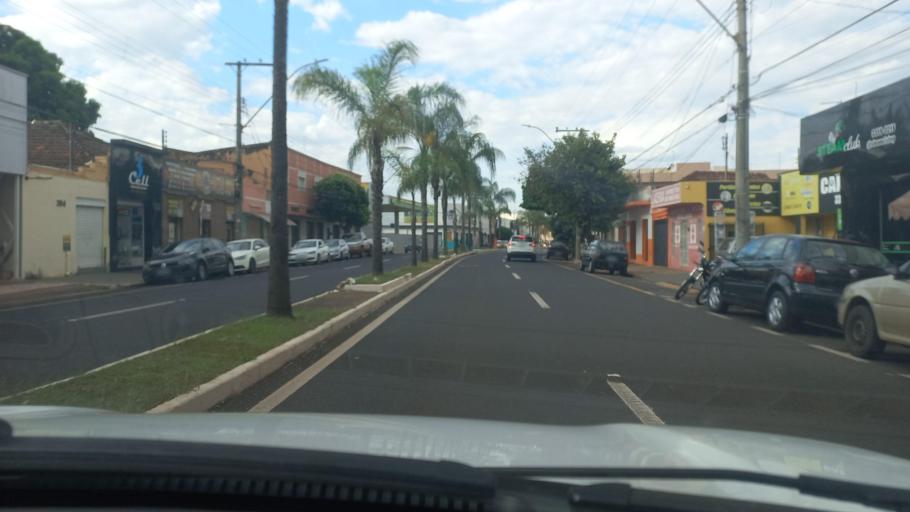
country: BR
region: Minas Gerais
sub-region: Uberaba
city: Uberaba
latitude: -19.7652
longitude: -47.9429
